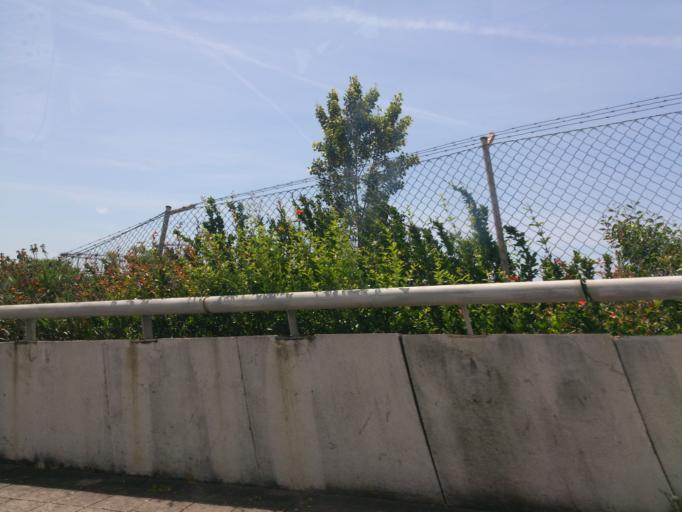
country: PT
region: Lisbon
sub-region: Loures
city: Moscavide
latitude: 38.7547
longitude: -9.1000
